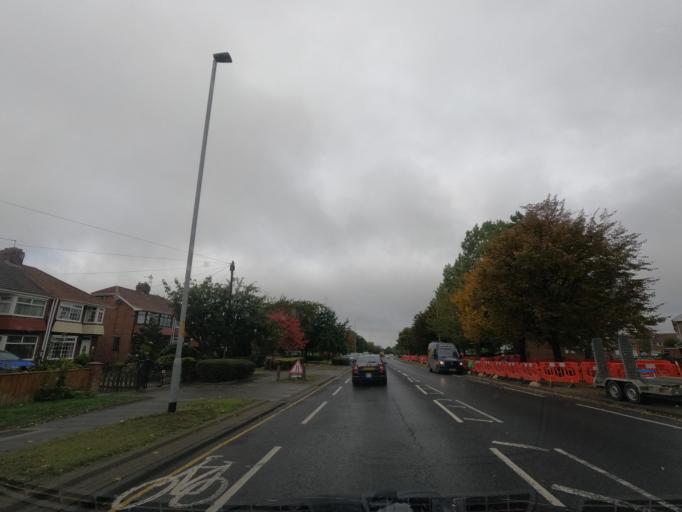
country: GB
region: England
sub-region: Middlesbrough
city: Nunthorpe
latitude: 54.5538
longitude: -1.1833
